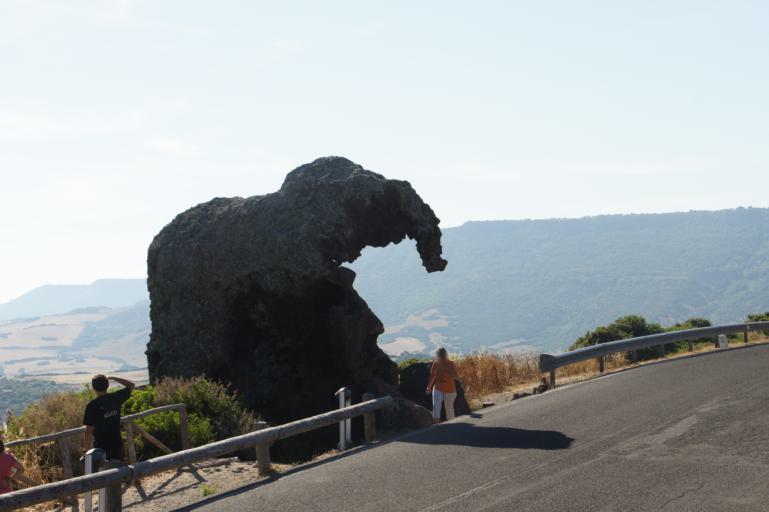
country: IT
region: Sardinia
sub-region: Provincia di Sassari
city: Castelsardo
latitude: 40.8898
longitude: 8.7455
